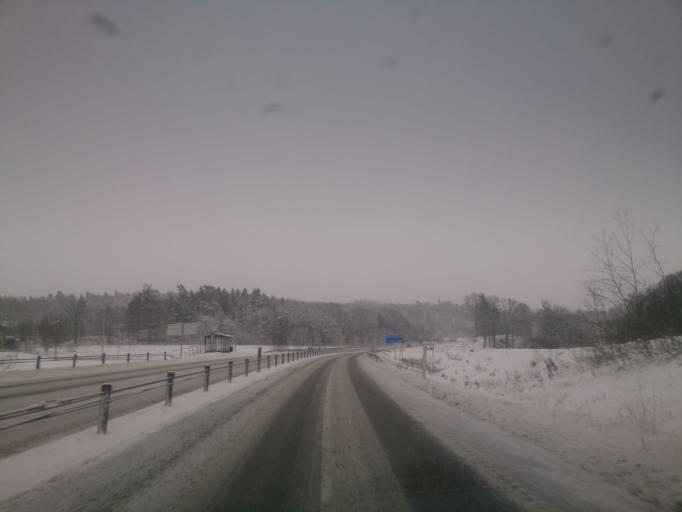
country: SE
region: OEstergoetland
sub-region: Norrkopings Kommun
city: Svartinge
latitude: 58.6931
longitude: 15.9199
